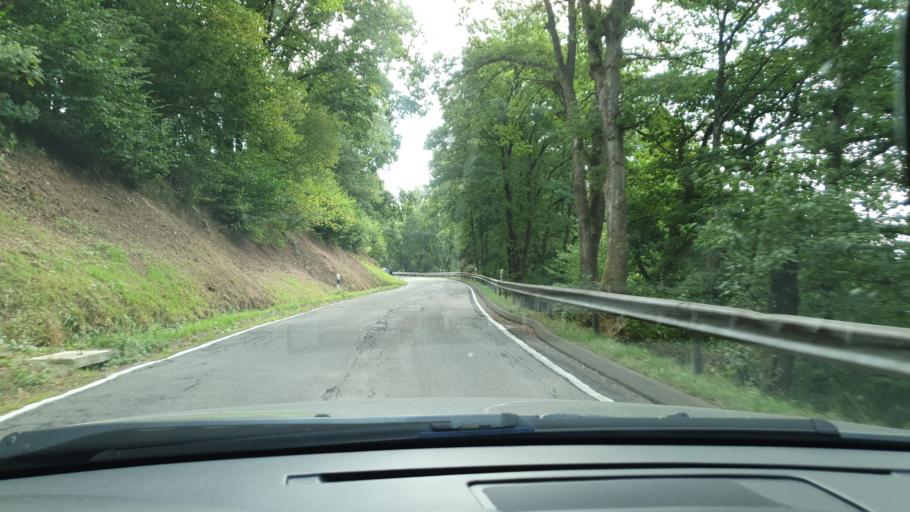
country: DE
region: Rheinland-Pfalz
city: Wiesbach
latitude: 49.3320
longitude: 7.4558
